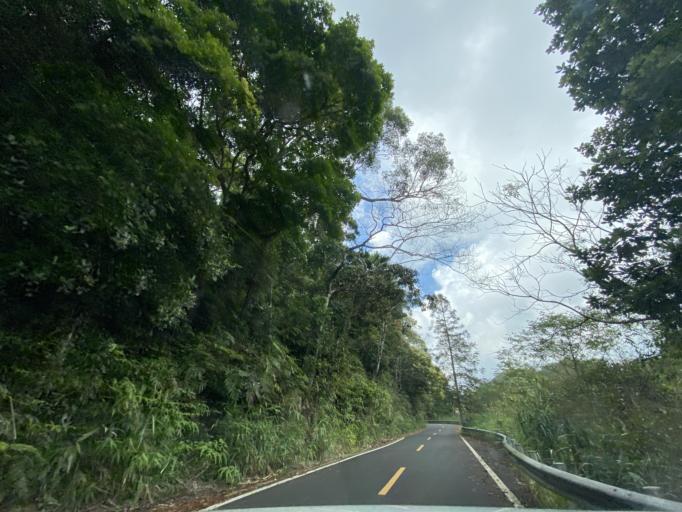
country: CN
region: Hainan
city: Diaoluoshan
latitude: 18.7160
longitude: 109.8801
